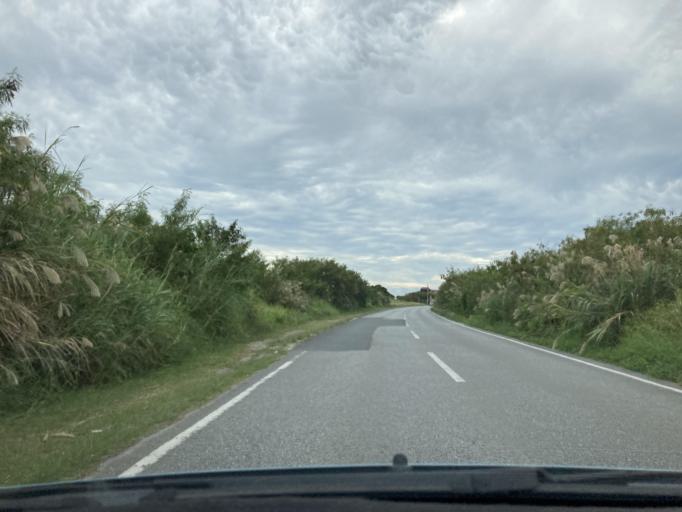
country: JP
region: Okinawa
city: Okinawa
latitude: 26.3892
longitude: 127.7410
